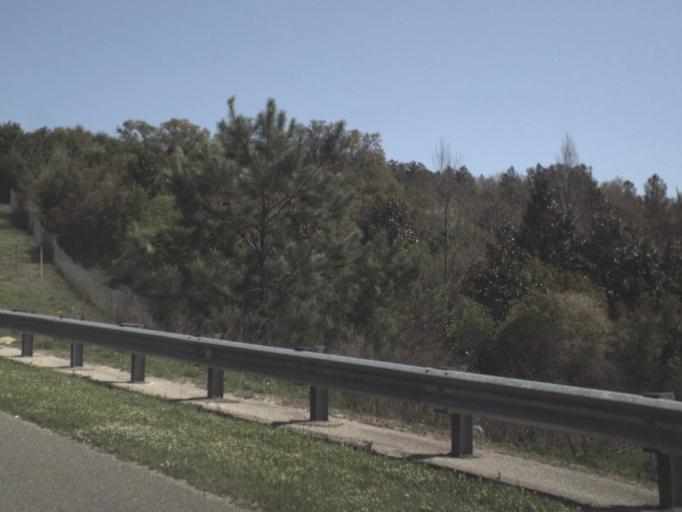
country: US
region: Florida
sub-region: Liberty County
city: Bristol
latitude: 30.4317
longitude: -84.9946
